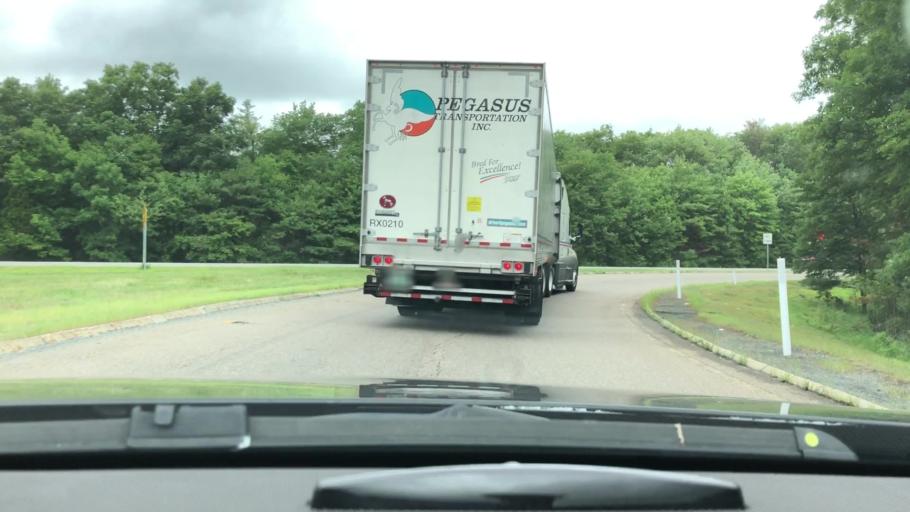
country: US
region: Massachusetts
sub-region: Bristol County
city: Mansfield Center
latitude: 42.0247
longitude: -71.2581
